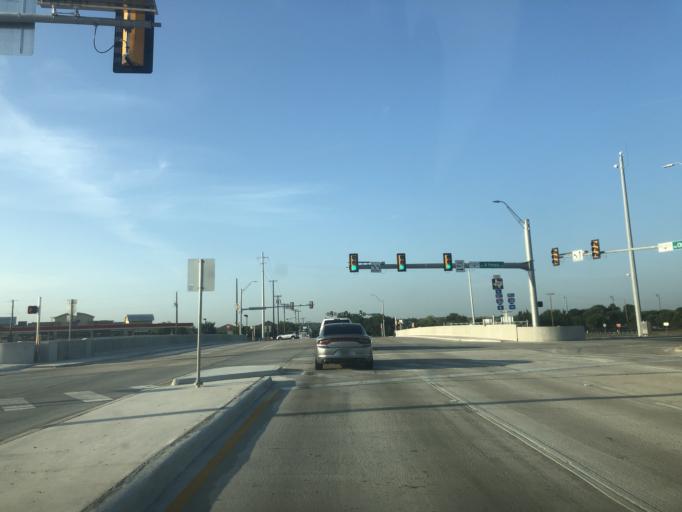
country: US
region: Texas
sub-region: Tarrant County
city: White Settlement
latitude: 32.7301
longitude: -97.5037
